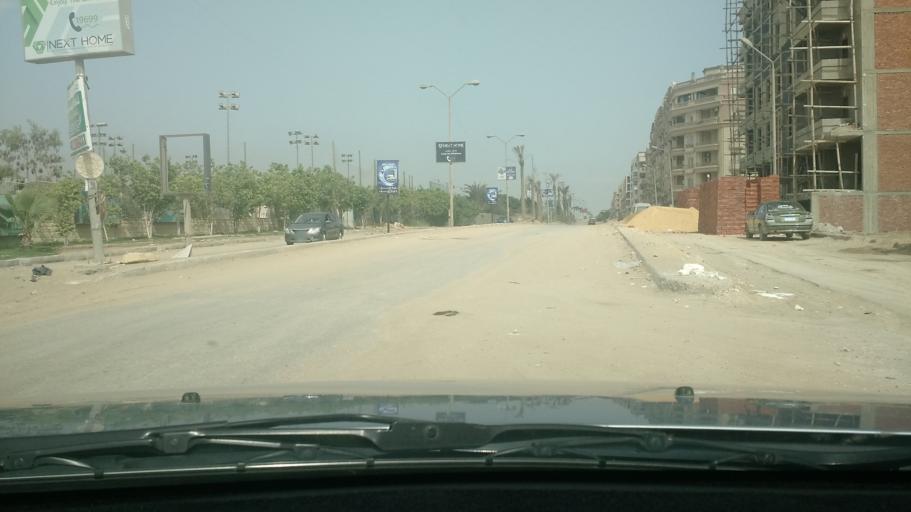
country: EG
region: Muhafazat al Qahirah
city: Cairo
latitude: 29.9932
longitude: 31.2976
